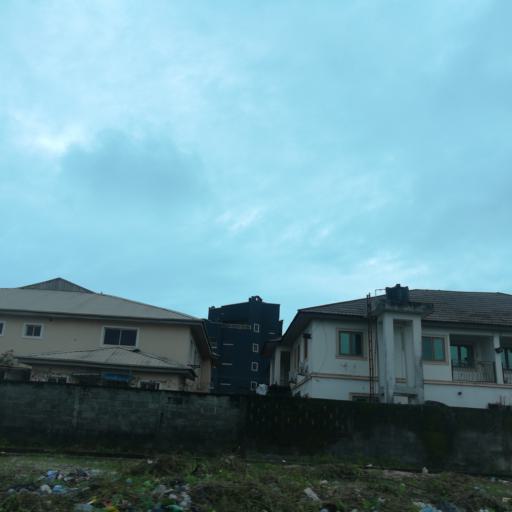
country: NG
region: Lagos
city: Ikoyi
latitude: 6.4371
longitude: 3.4732
